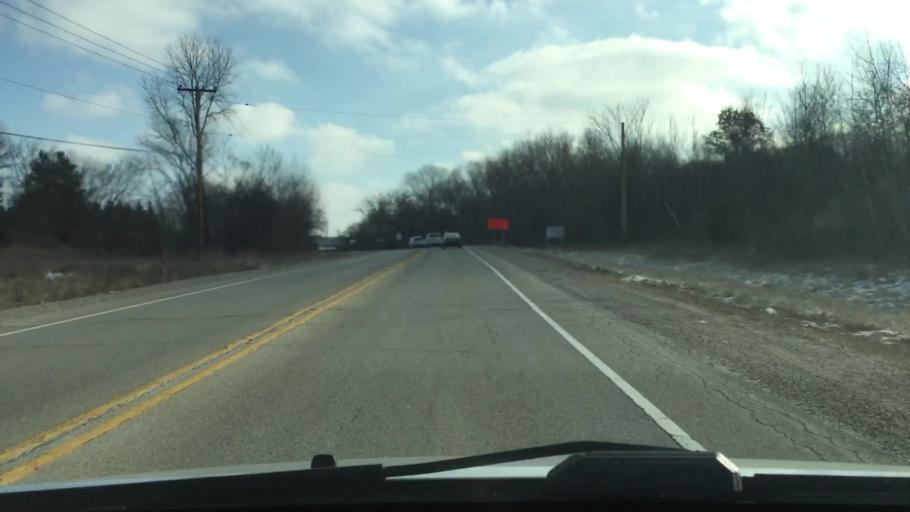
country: US
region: Wisconsin
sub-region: Waukesha County
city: Wales
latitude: 43.0110
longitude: -88.3911
